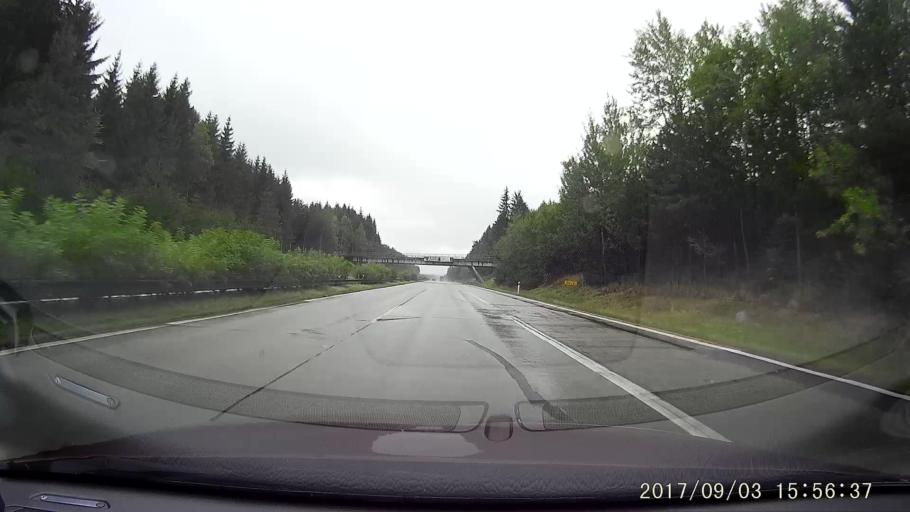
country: CZ
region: Vysocina
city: Heralec
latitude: 49.4883
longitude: 15.5124
